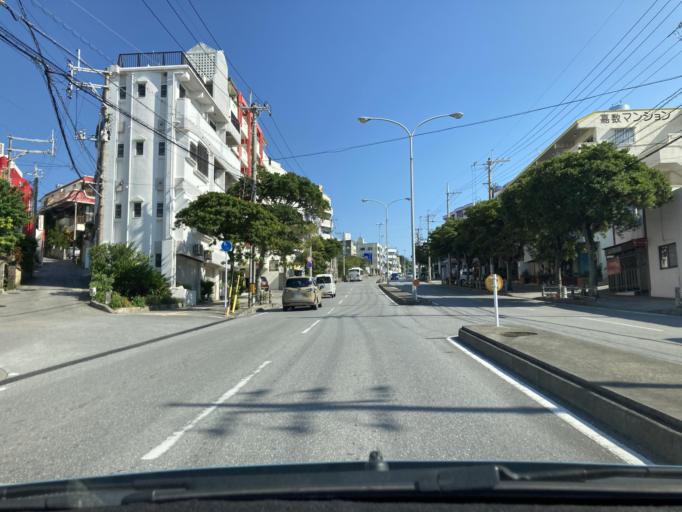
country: JP
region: Okinawa
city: Naha-shi
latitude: 26.2049
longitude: 127.7037
